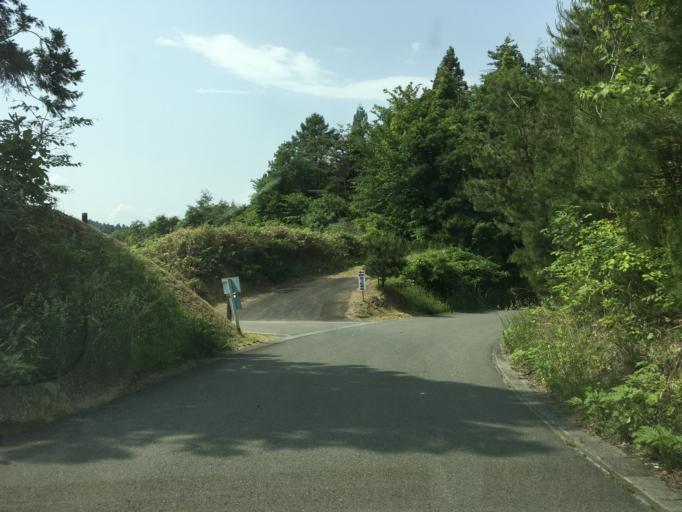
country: JP
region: Iwate
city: Hanamaki
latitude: 39.3965
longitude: 141.1723
